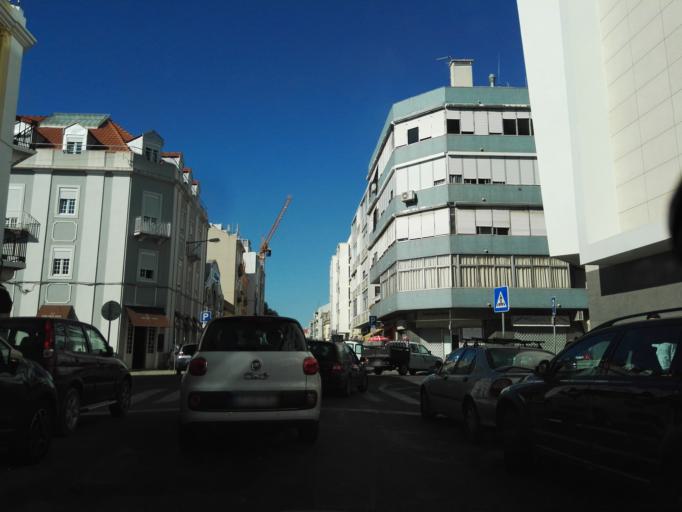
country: PT
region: Lisbon
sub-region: Lisbon
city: Lisbon
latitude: 38.7172
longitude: -9.1664
